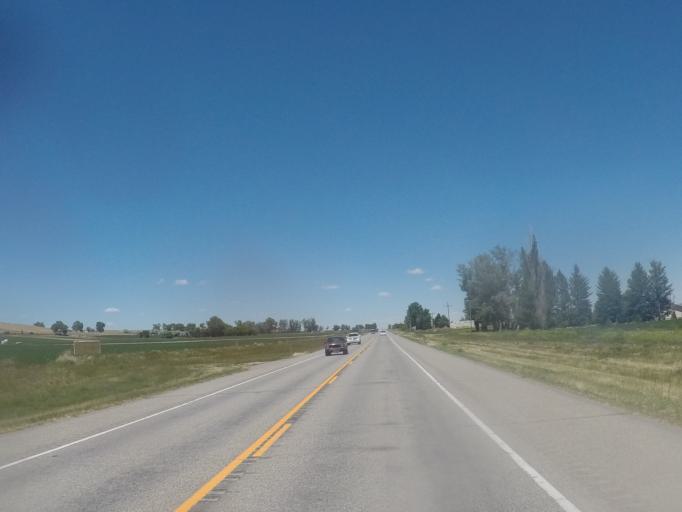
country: US
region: Montana
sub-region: Yellowstone County
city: Laurel
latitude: 45.4689
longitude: -108.8630
